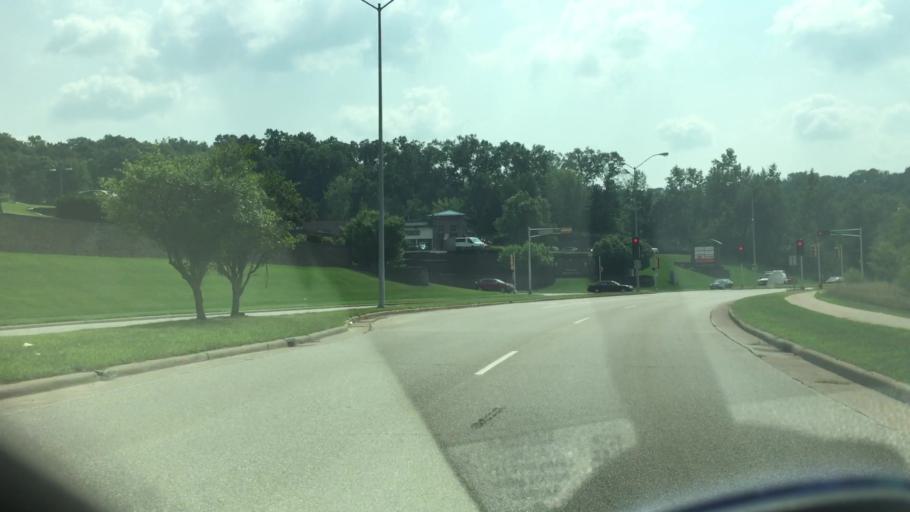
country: US
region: Wisconsin
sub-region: Eau Claire County
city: Altoona
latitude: 44.7727
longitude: -91.4380
